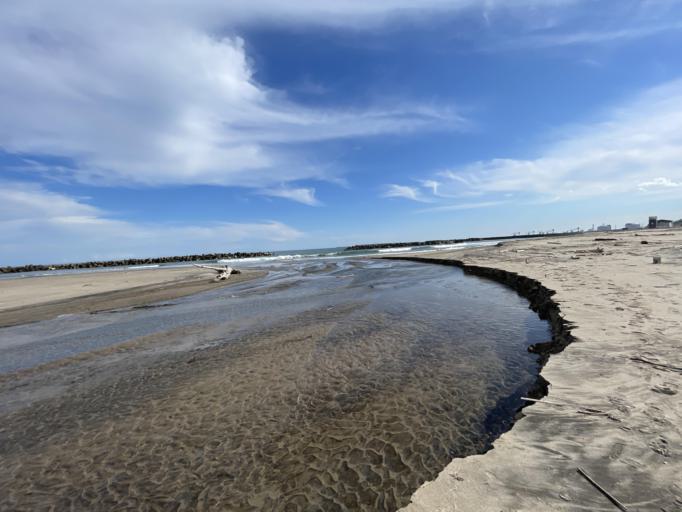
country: JP
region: Miyagi
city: Marumori
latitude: 37.8792
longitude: 140.9336
